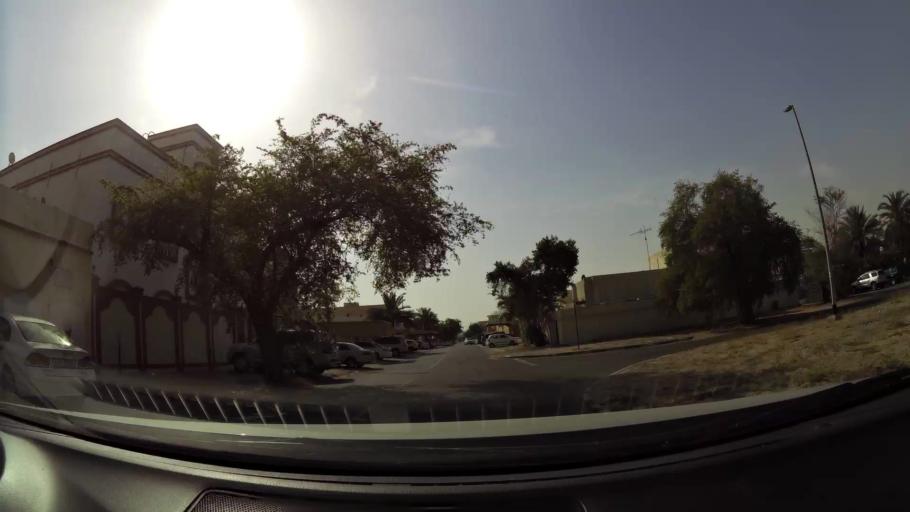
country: AE
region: Ash Shariqah
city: Sharjah
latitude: 25.2221
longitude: 55.3933
